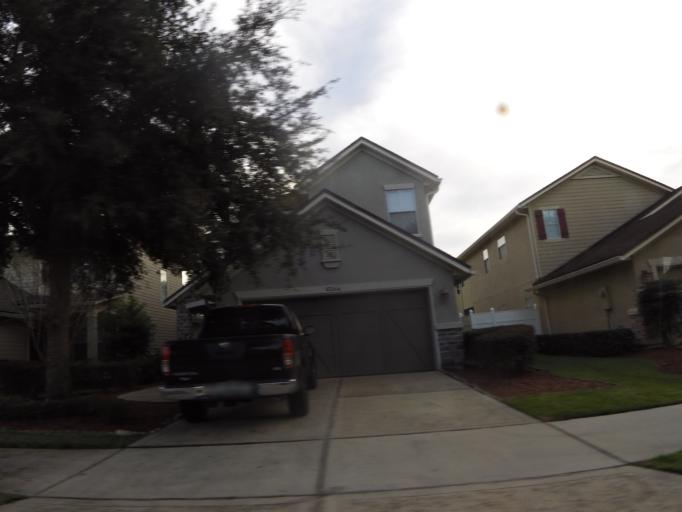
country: US
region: Florida
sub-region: Saint Johns County
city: Fruit Cove
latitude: 30.1578
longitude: -81.5472
